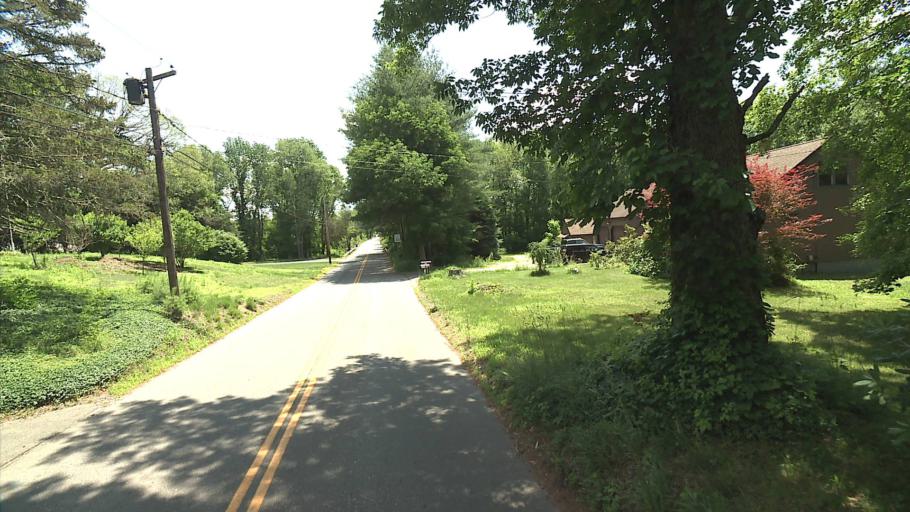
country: US
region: Connecticut
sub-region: New London County
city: Jewett City
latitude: 41.6125
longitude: -71.9341
